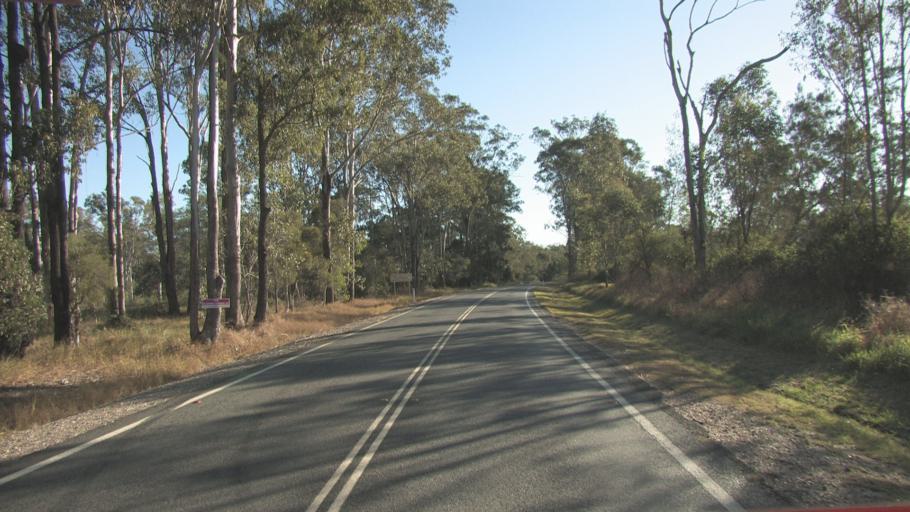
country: AU
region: Queensland
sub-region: Logan
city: Chambers Flat
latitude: -27.7806
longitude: 153.0649
